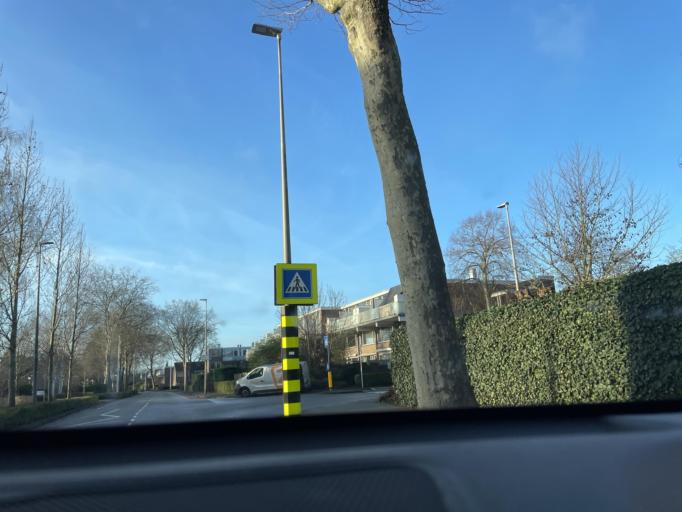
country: NL
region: South Holland
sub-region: Gemeente Krimpen aan den IJssel
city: Krimpen aan den IJssel
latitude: 51.9340
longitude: 4.6138
